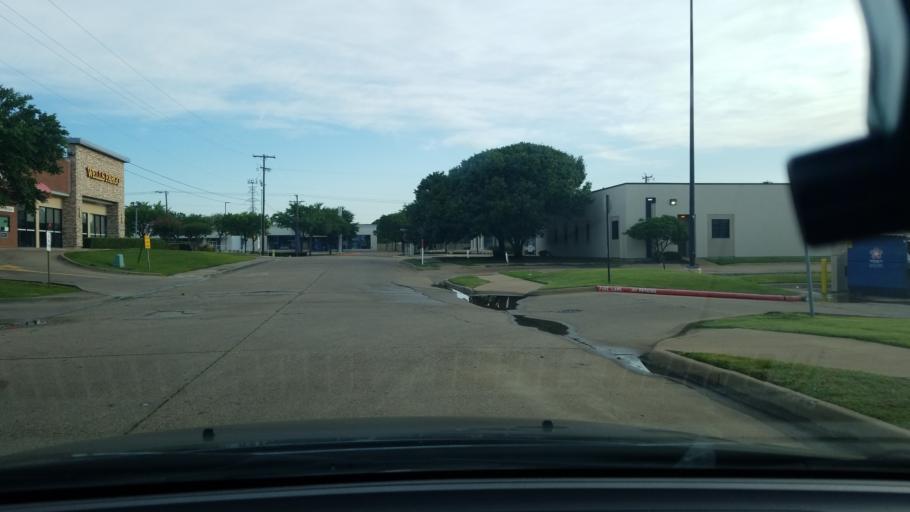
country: US
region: Texas
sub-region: Dallas County
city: Mesquite
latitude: 32.8099
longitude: -96.6146
